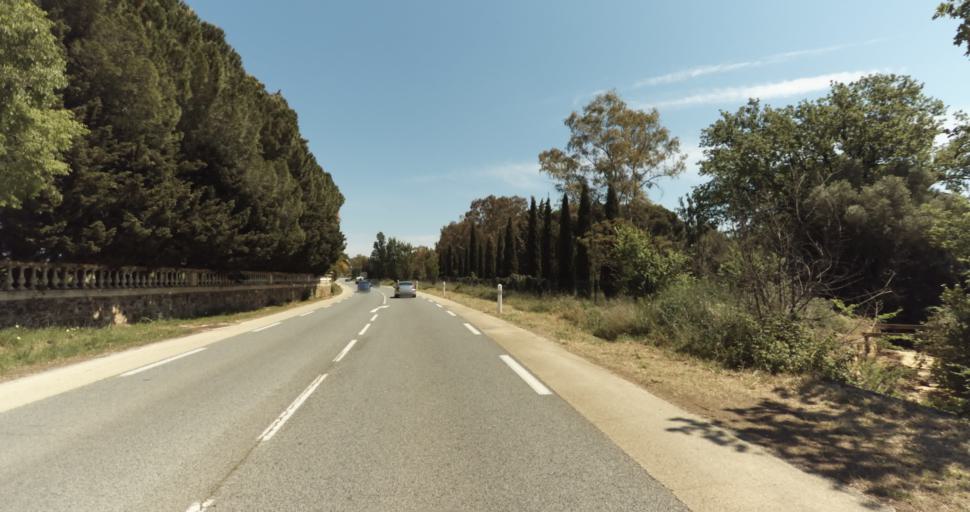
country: FR
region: Provence-Alpes-Cote d'Azur
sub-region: Departement du Var
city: Hyeres
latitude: 43.1279
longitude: 6.1861
